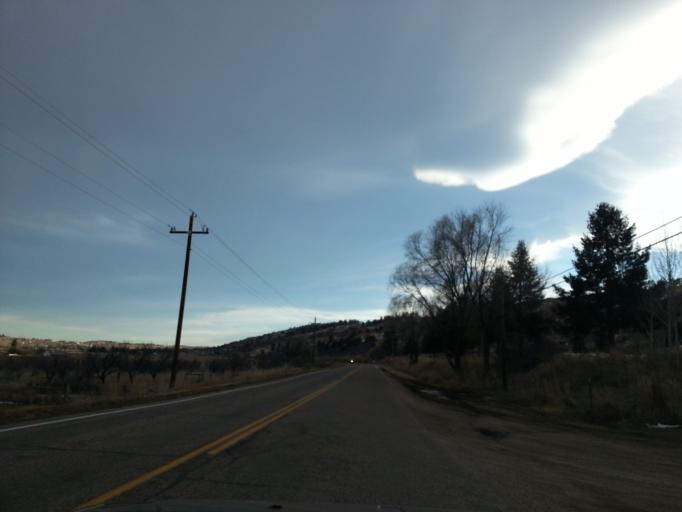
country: US
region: Colorado
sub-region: Larimer County
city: Loveland
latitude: 40.4533
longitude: -105.2047
